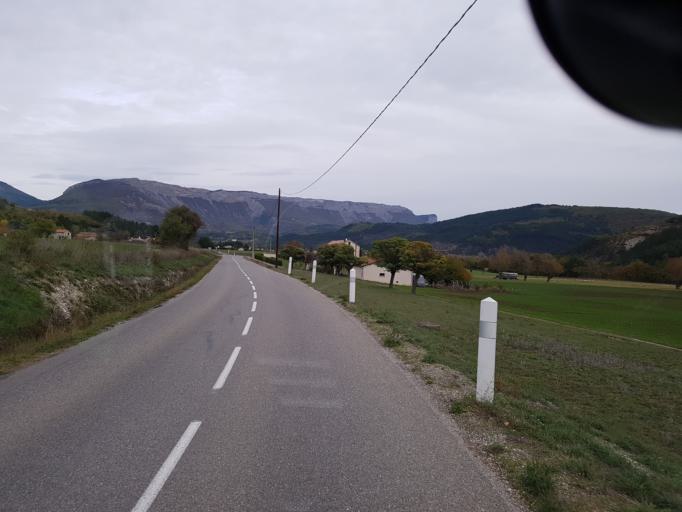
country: FR
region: Provence-Alpes-Cote d'Azur
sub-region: Departement des Hautes-Alpes
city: Laragne-Monteglin
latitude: 44.3370
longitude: 5.7566
